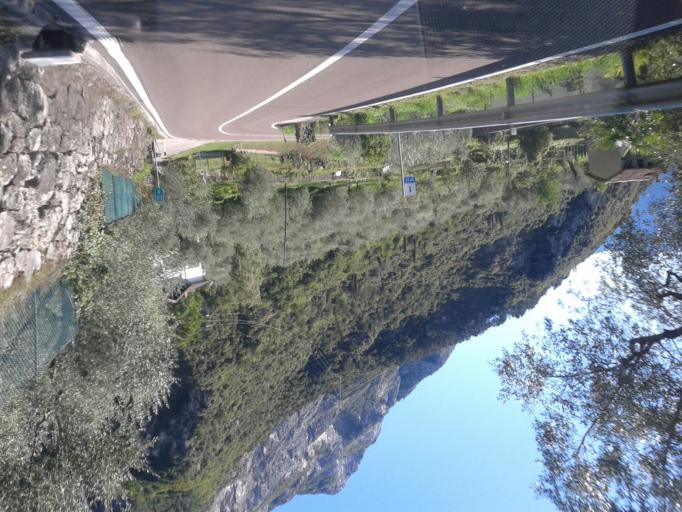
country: IT
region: Trentino-Alto Adige
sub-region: Provincia di Trento
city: Riva del Garda
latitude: 45.8993
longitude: 10.8344
